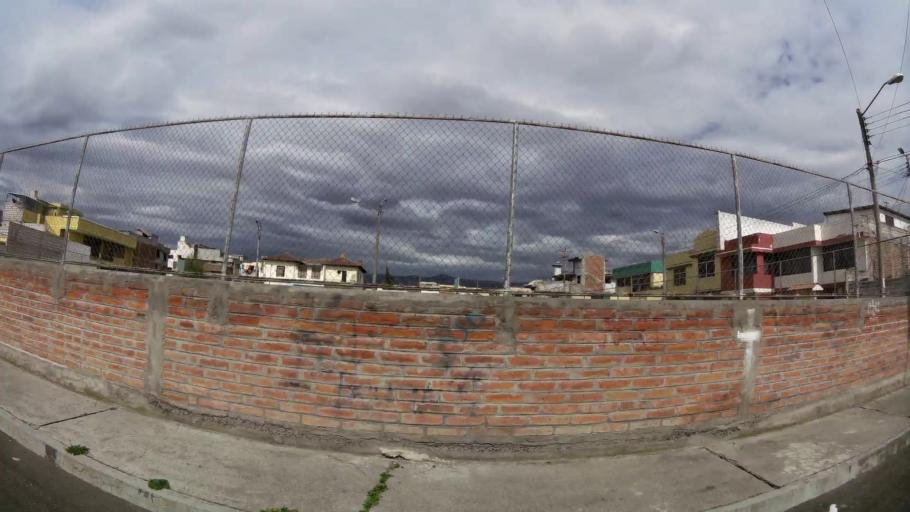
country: EC
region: Cotopaxi
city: Latacunga
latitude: -0.9239
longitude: -78.6216
